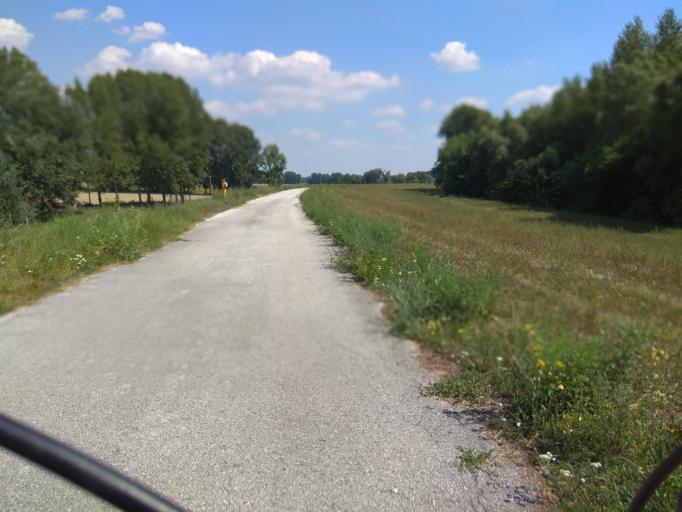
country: SK
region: Trnavsky
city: Gabcikovo
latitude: 47.8174
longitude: 17.6236
